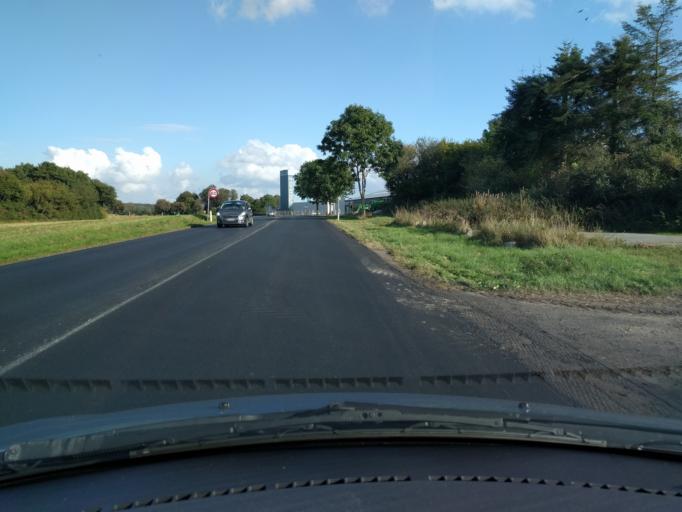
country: DK
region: South Denmark
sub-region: Assens Kommune
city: Glamsbjerg
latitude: 55.2695
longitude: 10.1202
